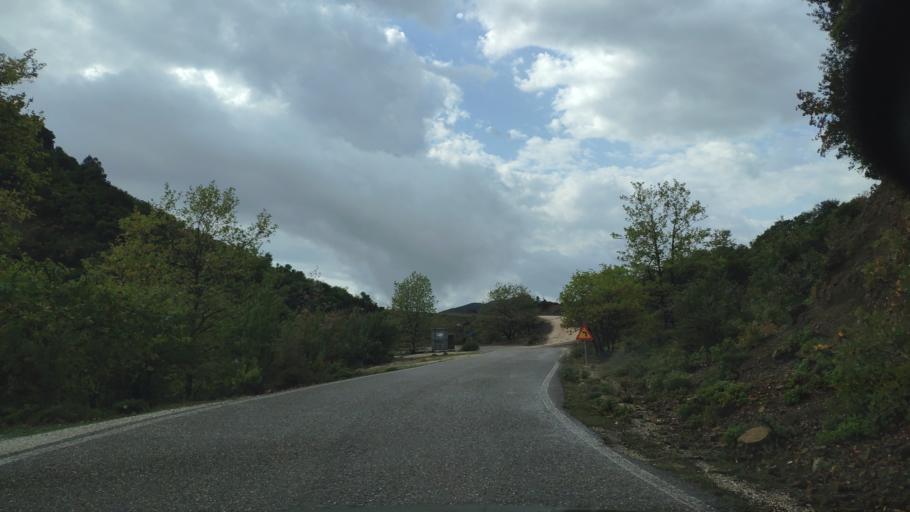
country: GR
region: West Greece
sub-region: Nomos Aitolias kai Akarnanias
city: Sardinia
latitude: 38.8547
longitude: 21.3068
